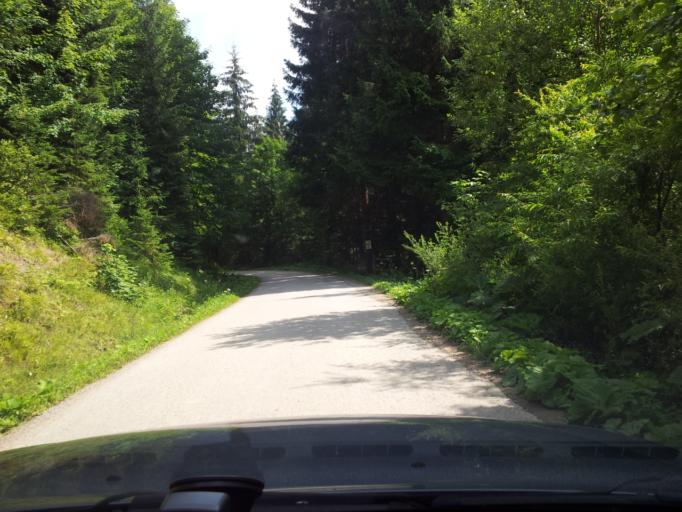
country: SK
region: Zilinsky
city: Oravska Lesna
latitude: 49.3866
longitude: 19.1804
